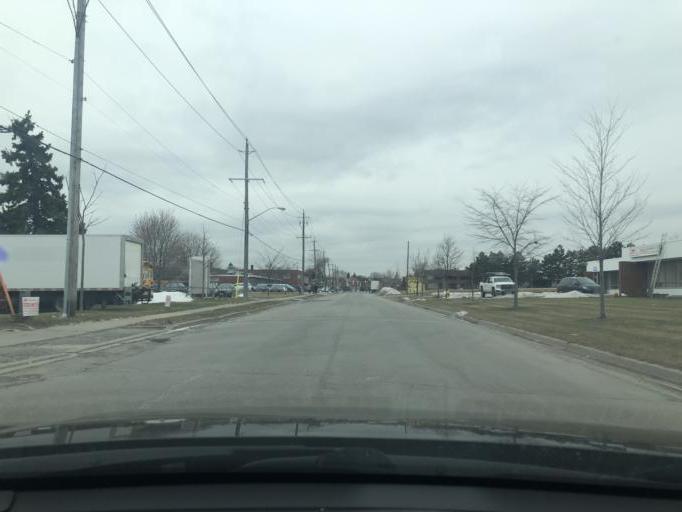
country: CA
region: Ontario
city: Scarborough
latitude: 43.7680
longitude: -79.2992
